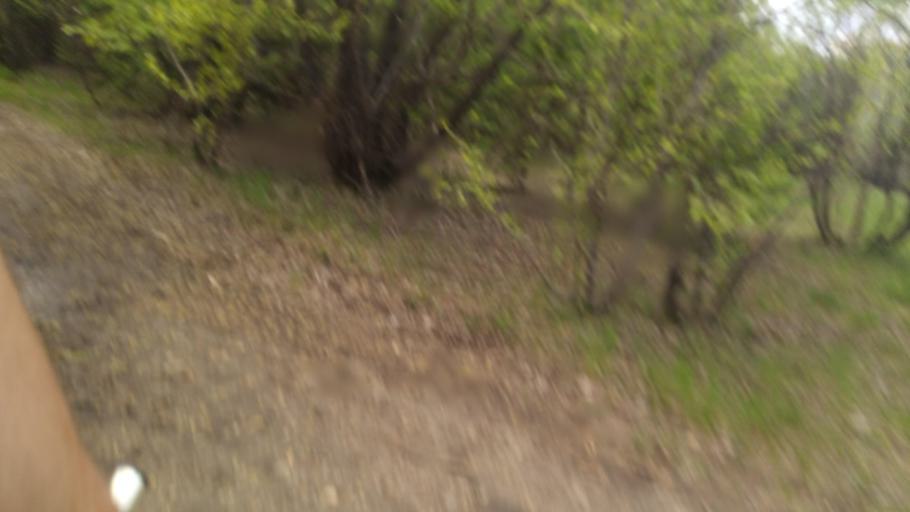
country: RU
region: Chelyabinsk
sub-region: Gorod Chelyabinsk
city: Chelyabinsk
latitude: 55.1691
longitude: 61.3408
